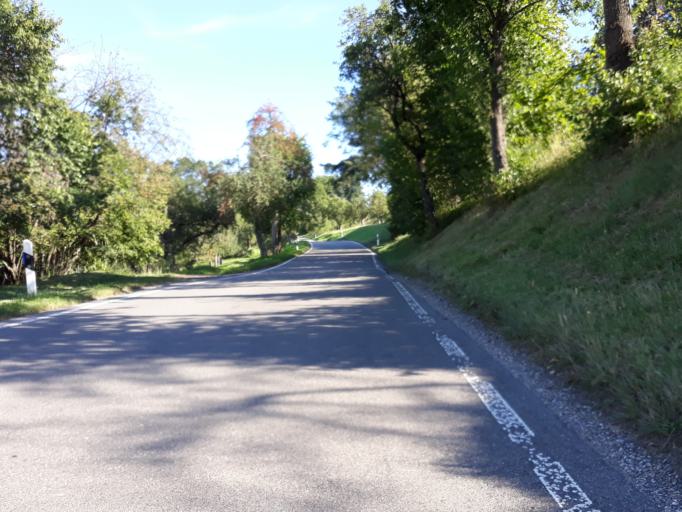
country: DE
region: Baden-Wuerttemberg
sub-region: Karlsruhe Region
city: Ostelsheim
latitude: 48.7227
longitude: 8.8496
